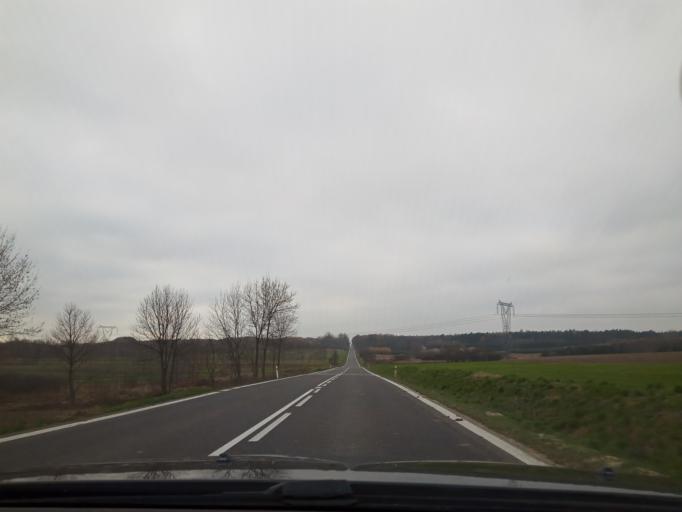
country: PL
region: Swietokrzyskie
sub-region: Powiat jedrzejowski
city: Imielno
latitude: 50.6075
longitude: 20.4851
